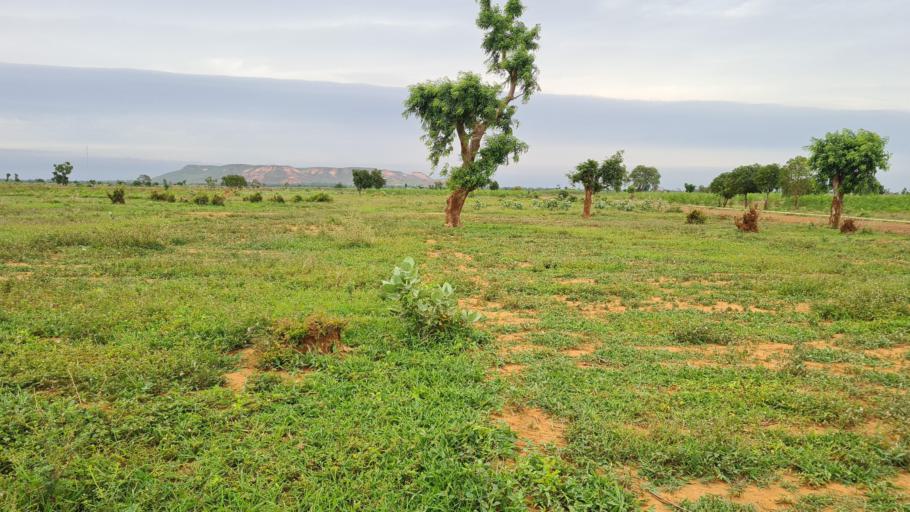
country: NE
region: Tahoua
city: Birni N Konni
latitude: 13.8345
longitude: 5.2671
